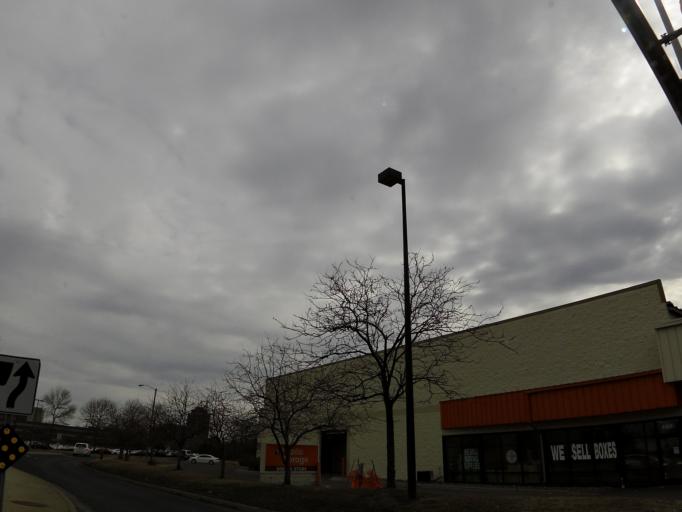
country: US
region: Minnesota
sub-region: Hennepin County
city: Edina
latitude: 44.8632
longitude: -93.3358
